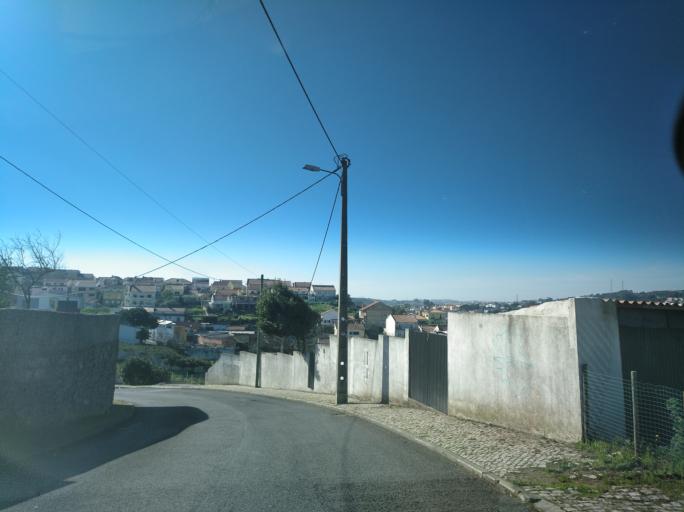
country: PT
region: Lisbon
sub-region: Odivelas
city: Canecas
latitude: 38.8101
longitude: -9.2205
